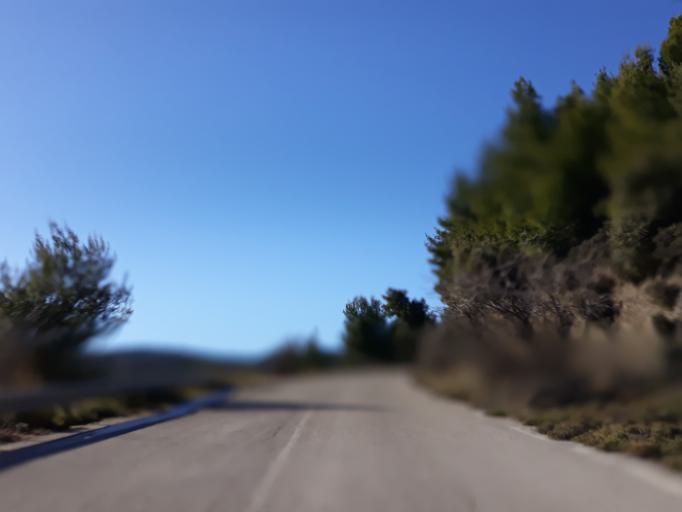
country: GR
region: Attica
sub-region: Nomarchia Dytikis Attikis
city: Fyli
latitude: 38.1450
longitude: 23.6422
